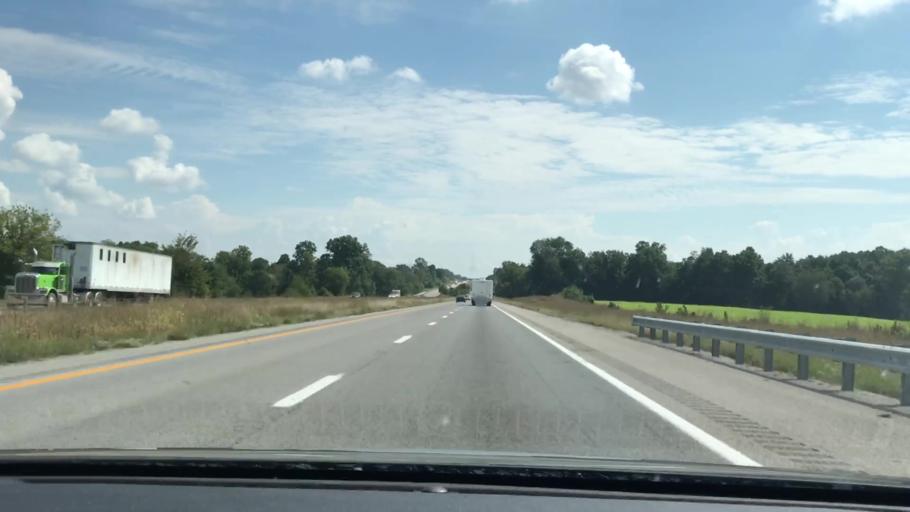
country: US
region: Kentucky
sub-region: Christian County
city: Hopkinsville
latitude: 36.7658
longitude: -87.5485
